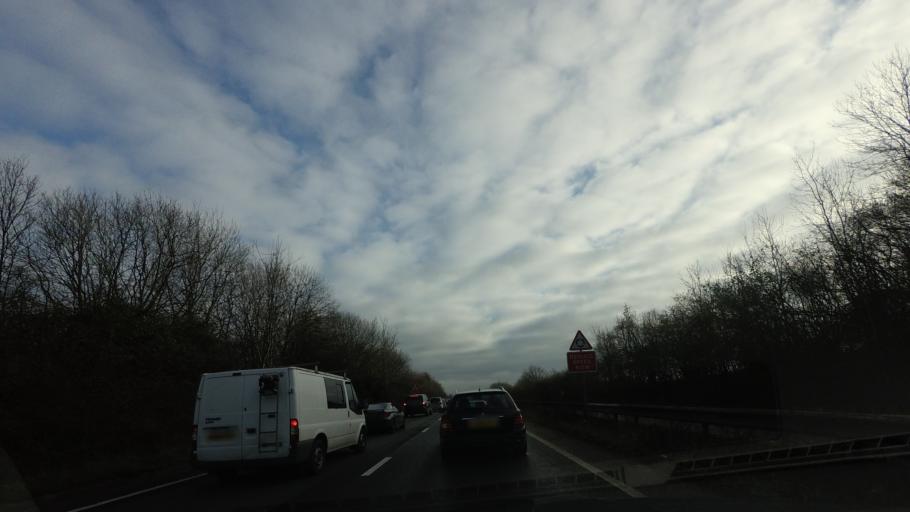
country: GB
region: England
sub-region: Kent
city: Pembury
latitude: 51.1373
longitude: 0.3425
